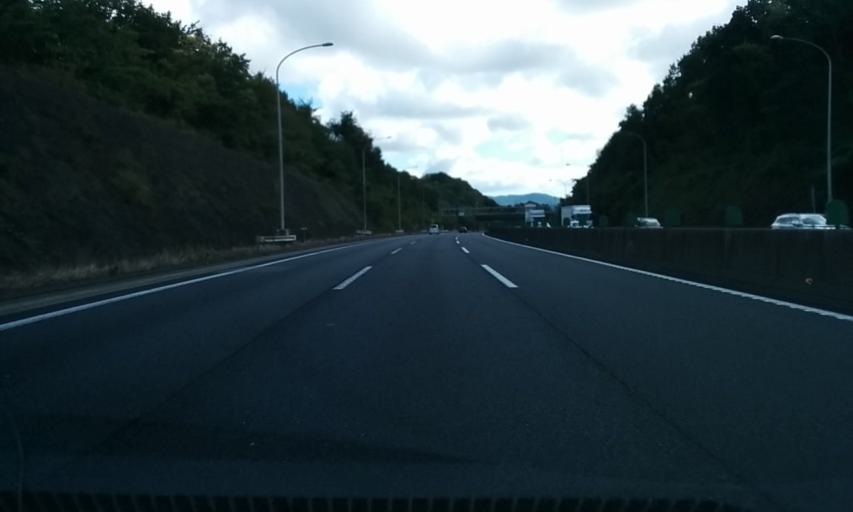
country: JP
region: Hyogo
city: Sandacho
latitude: 34.8358
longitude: 135.2694
